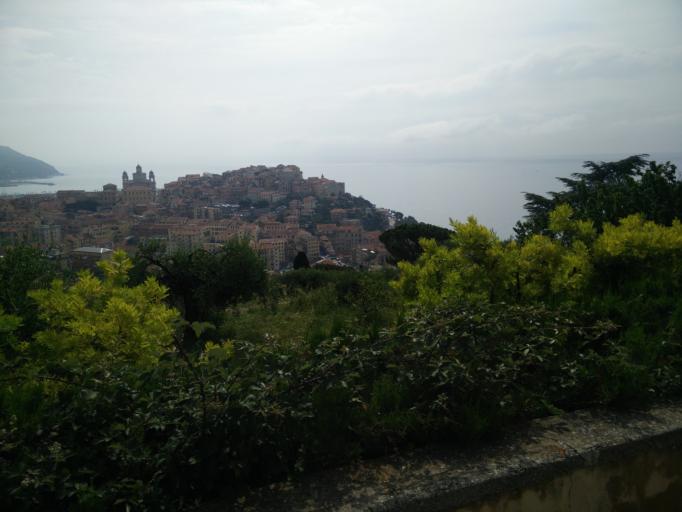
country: IT
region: Liguria
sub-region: Provincia di Imperia
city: Imperia
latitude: 43.8738
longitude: 8.0053
